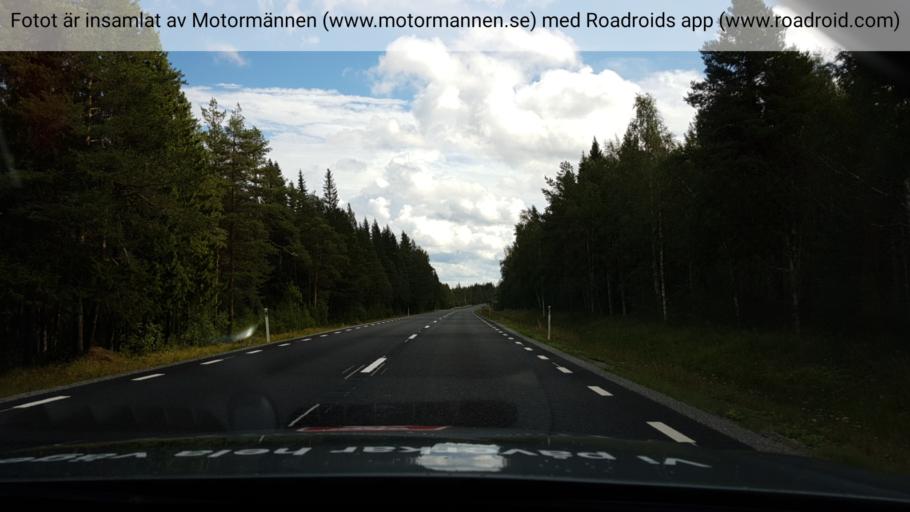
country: SE
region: Jaemtland
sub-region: OEstersunds Kommun
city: Lit
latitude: 63.2027
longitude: 14.9227
